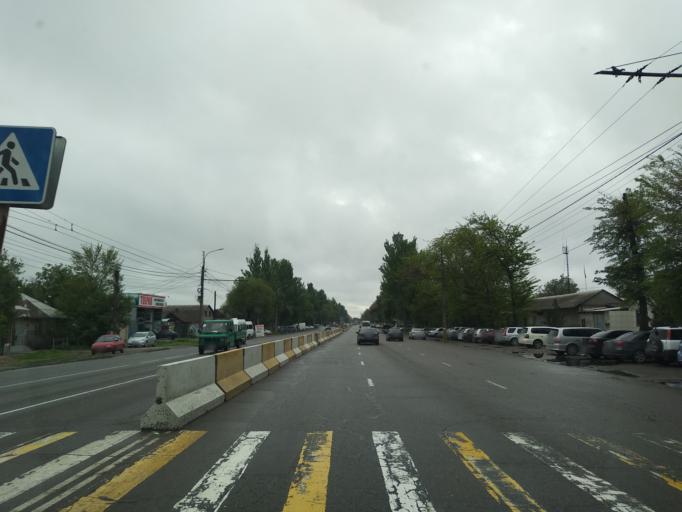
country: KG
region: Chuy
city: Lebedinovka
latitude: 42.8886
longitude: 74.6445
